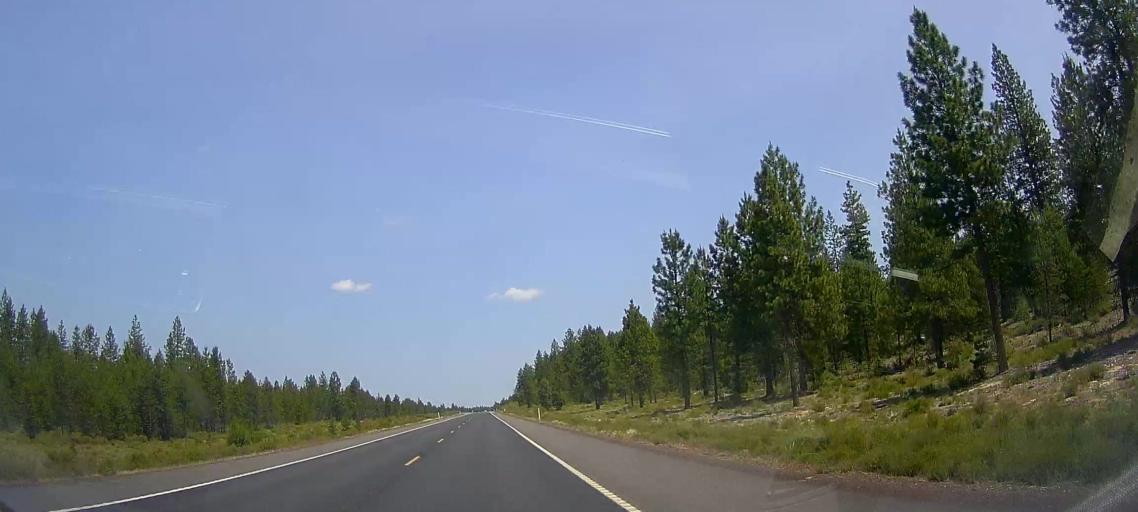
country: US
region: Oregon
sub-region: Deschutes County
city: La Pine
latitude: 43.5113
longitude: -121.6576
